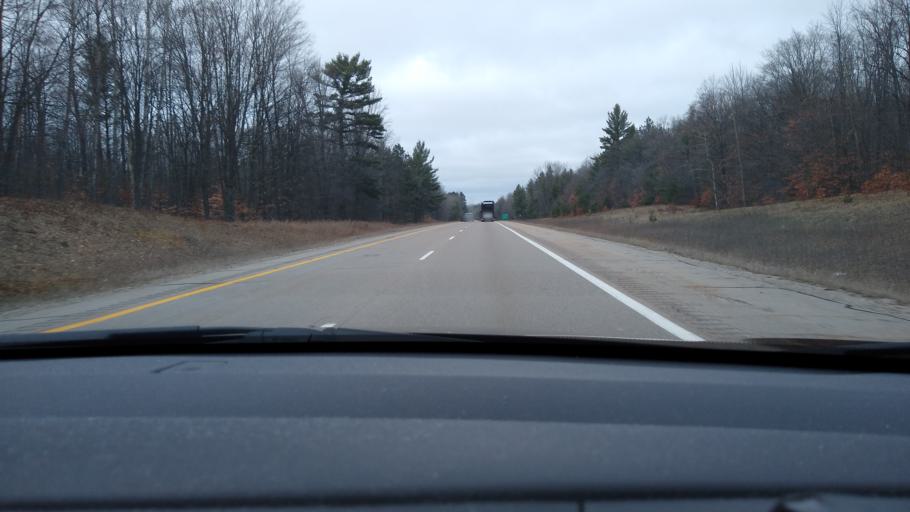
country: US
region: Michigan
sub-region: Crawford County
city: Grayling
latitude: 44.7614
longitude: -84.7087
